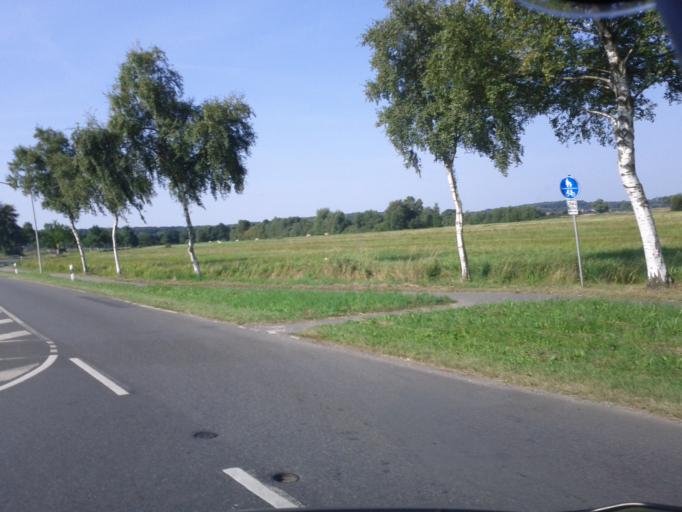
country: DE
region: Lower Saxony
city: Buxtehude
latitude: 53.4923
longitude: 9.6525
